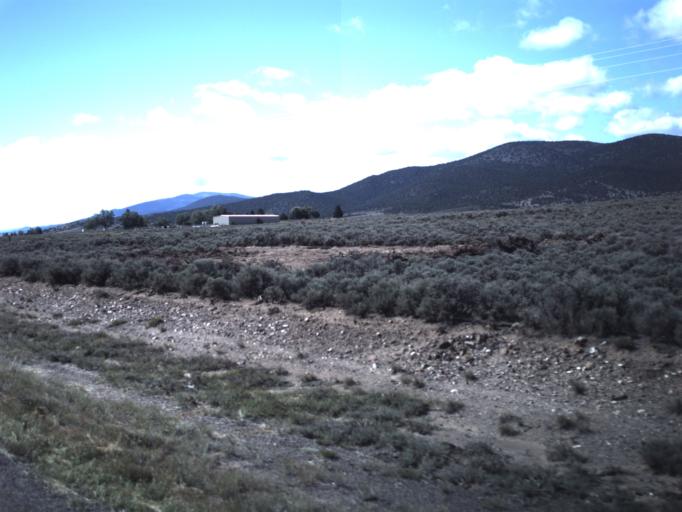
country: US
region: Utah
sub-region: Sevier County
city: Monroe
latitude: 38.5248
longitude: -111.8807
